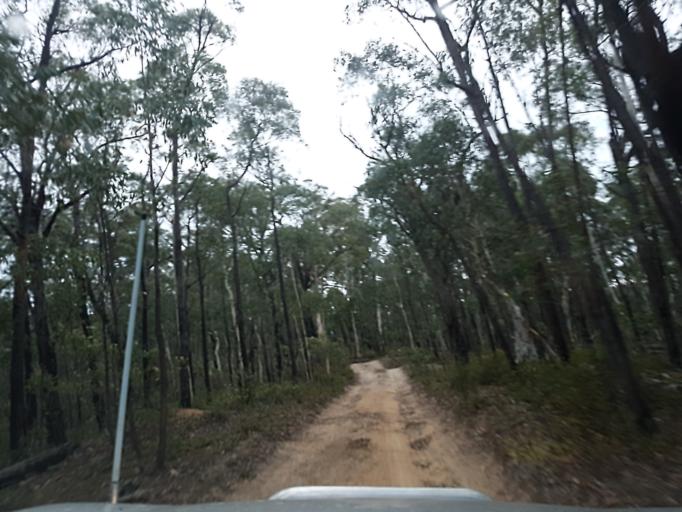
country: AU
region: New South Wales
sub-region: Snowy River
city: Jindabyne
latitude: -36.8514
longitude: 148.2273
